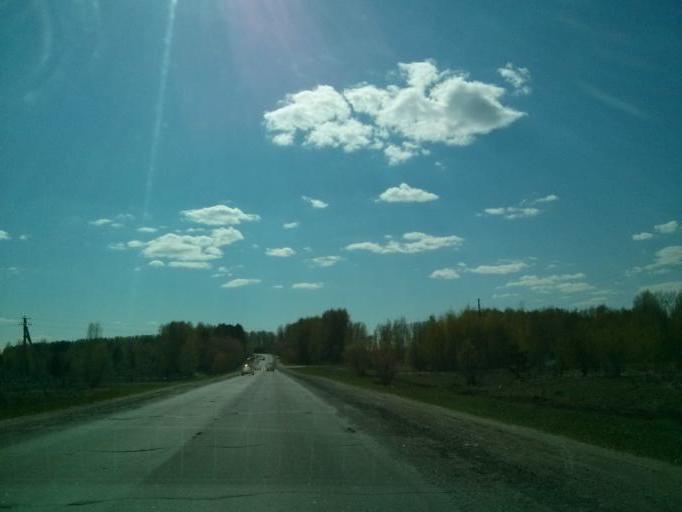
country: RU
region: Nizjnij Novgorod
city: Taremskoye
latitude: 55.9177
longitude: 43.0282
